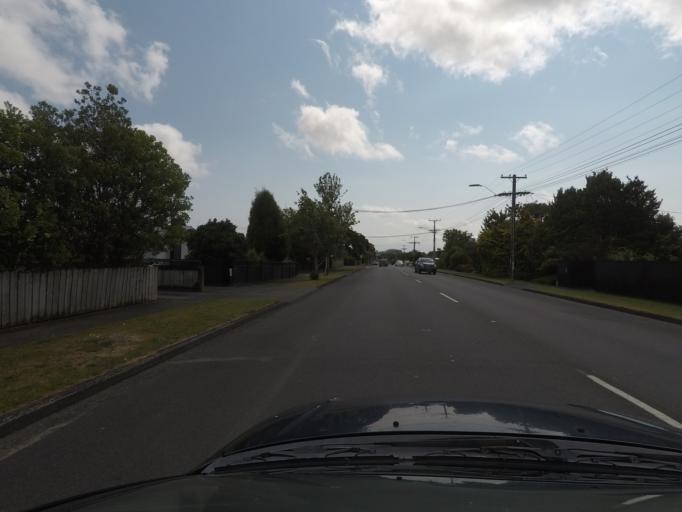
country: NZ
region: Northland
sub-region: Whangarei
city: Whangarei
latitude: -35.6875
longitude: 174.3245
